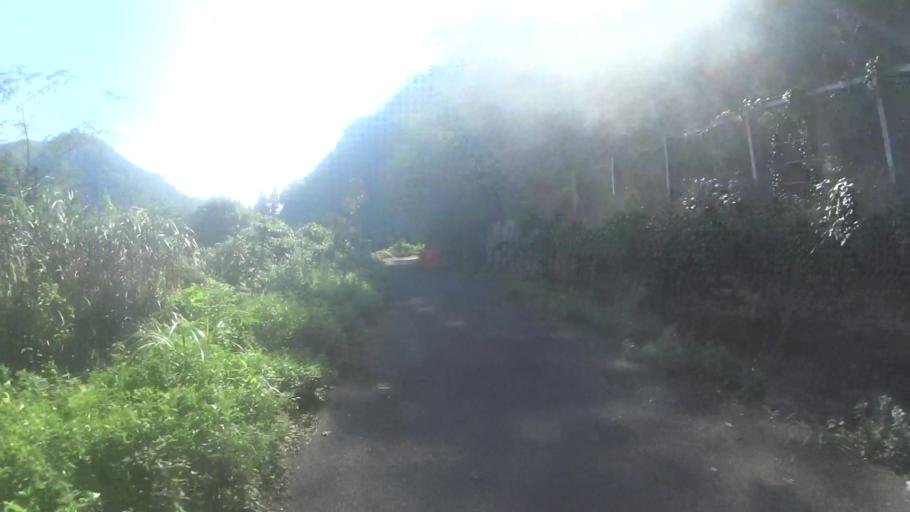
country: JP
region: Kyoto
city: Miyazu
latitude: 35.7090
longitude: 135.1584
